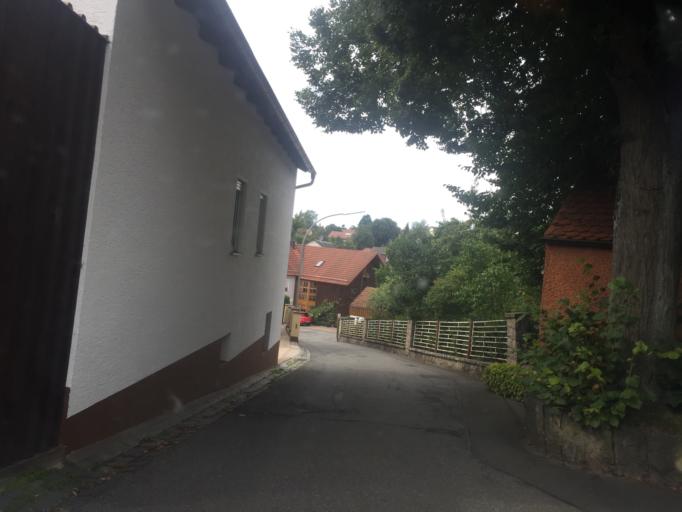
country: DE
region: Bavaria
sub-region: Upper Palatinate
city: Pressath
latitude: 49.7692
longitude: 11.9393
